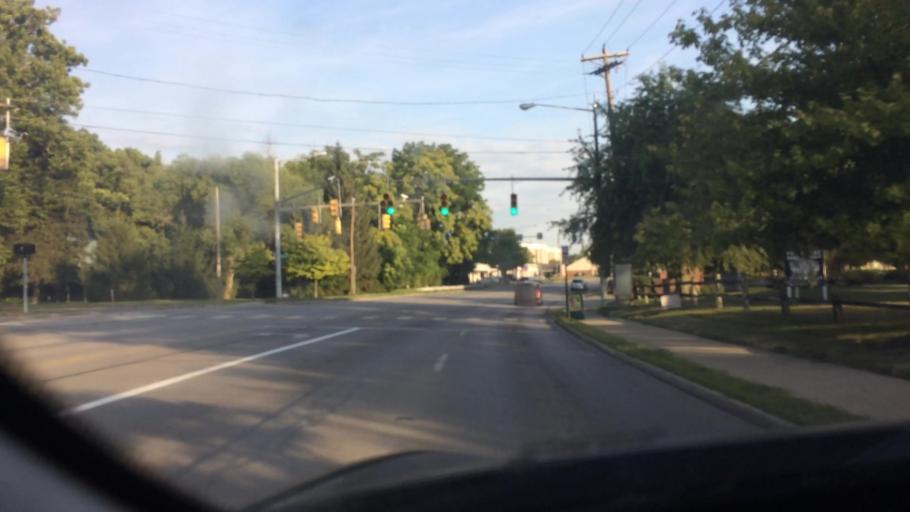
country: US
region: Ohio
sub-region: Lucas County
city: Sylvania
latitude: 41.7103
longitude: -83.6785
